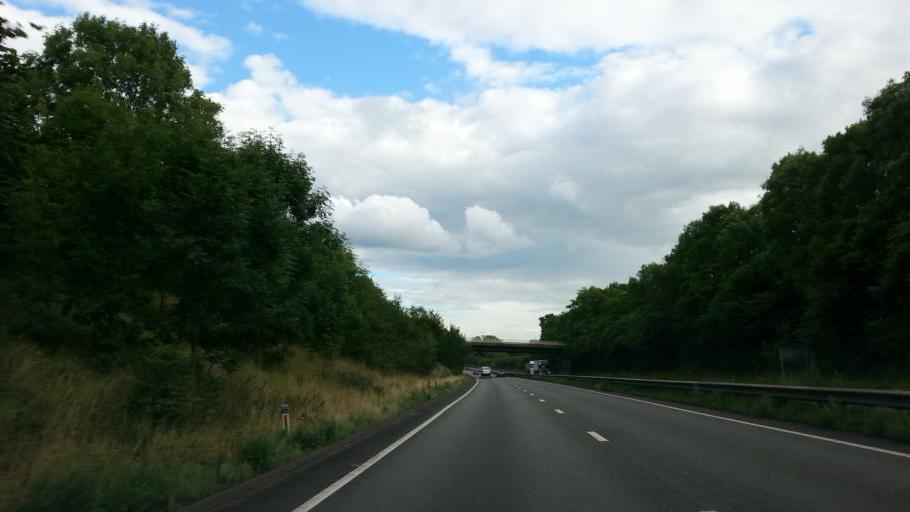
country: GB
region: England
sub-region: Nottinghamshire
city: Tuxford
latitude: 53.2382
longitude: -0.9000
